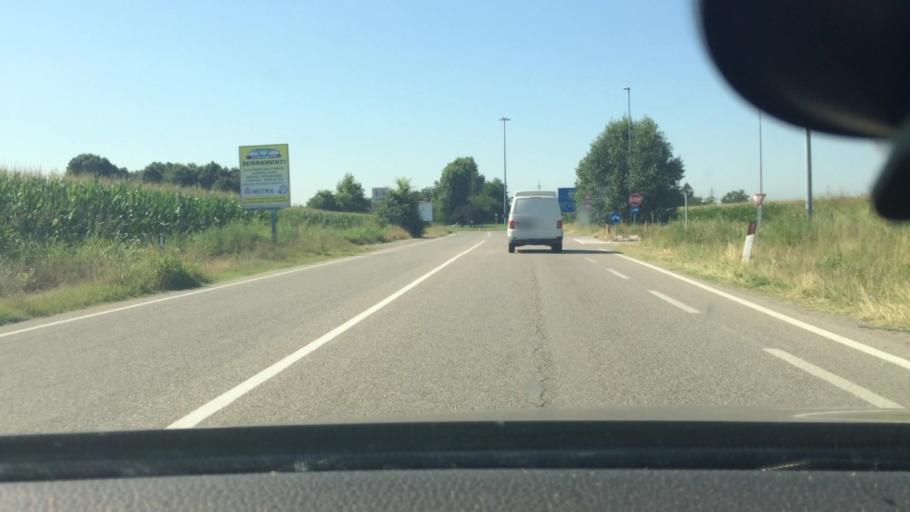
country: IT
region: Lombardy
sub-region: Citta metropolitana di Milano
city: Ossona
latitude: 45.5047
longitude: 8.9084
